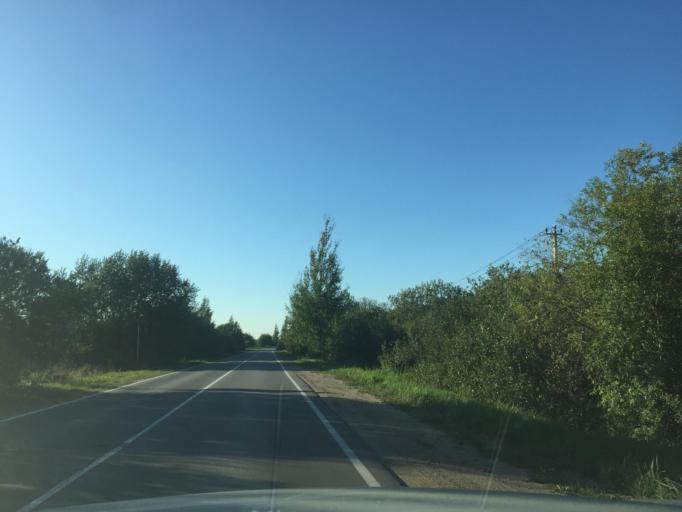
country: RU
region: Leningrad
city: Siverskiy
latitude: 59.3297
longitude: 30.0317
